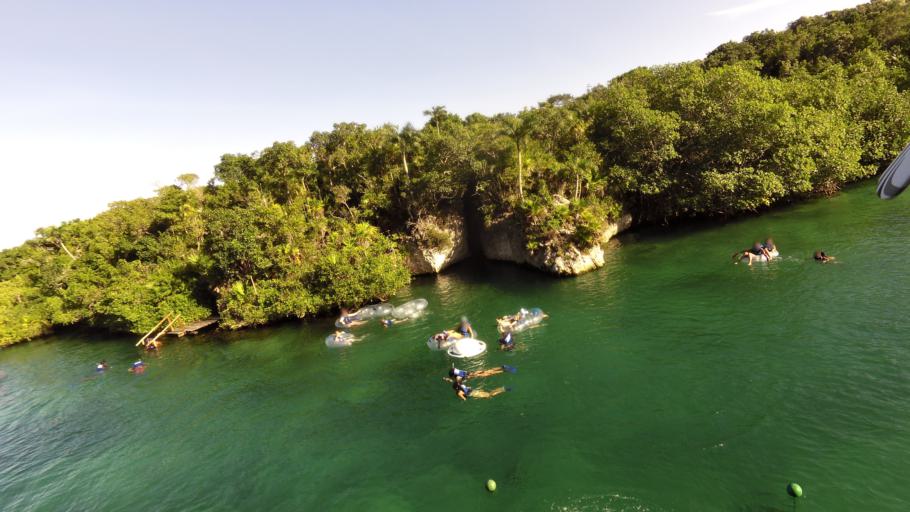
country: MX
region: Quintana Roo
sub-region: Tulum
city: Ciudad Chemuyil
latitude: 20.3165
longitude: -87.3606
